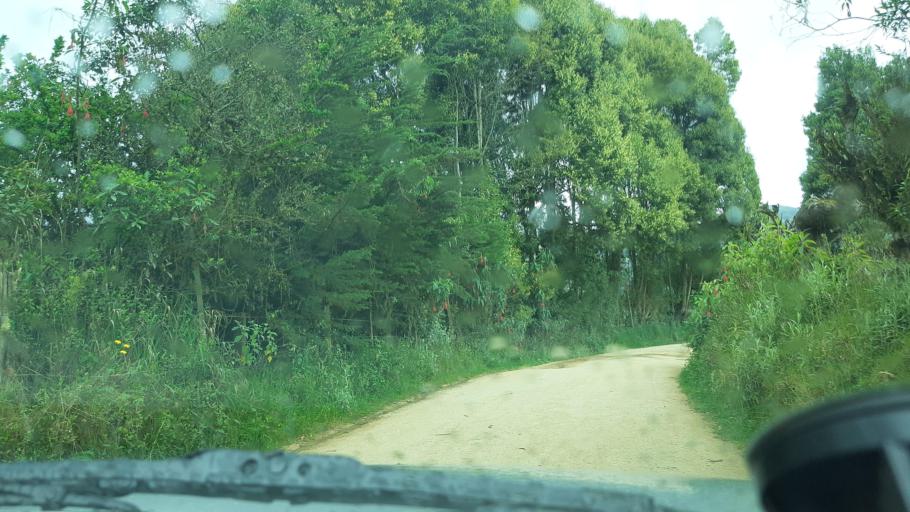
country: CO
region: Cundinamarca
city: Umbita
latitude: 5.2464
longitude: -73.4676
